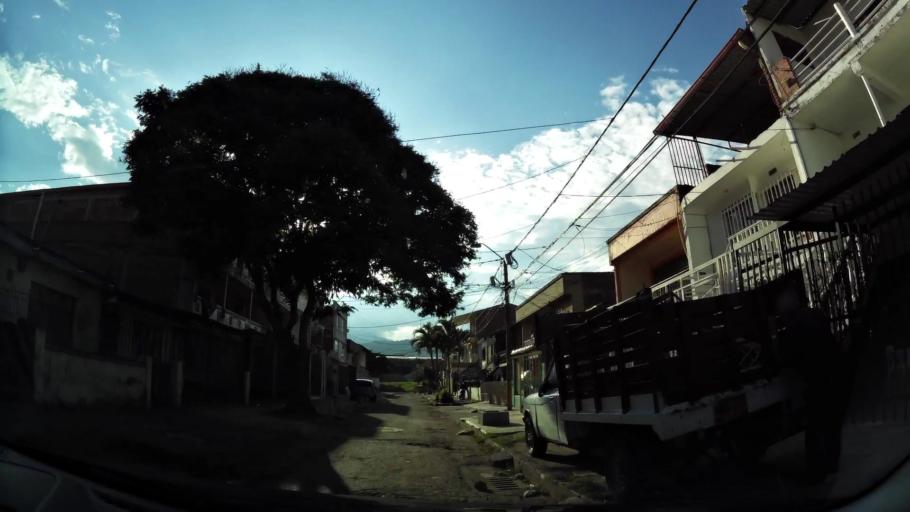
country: CO
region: Valle del Cauca
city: Cali
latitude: 3.4313
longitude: -76.5189
